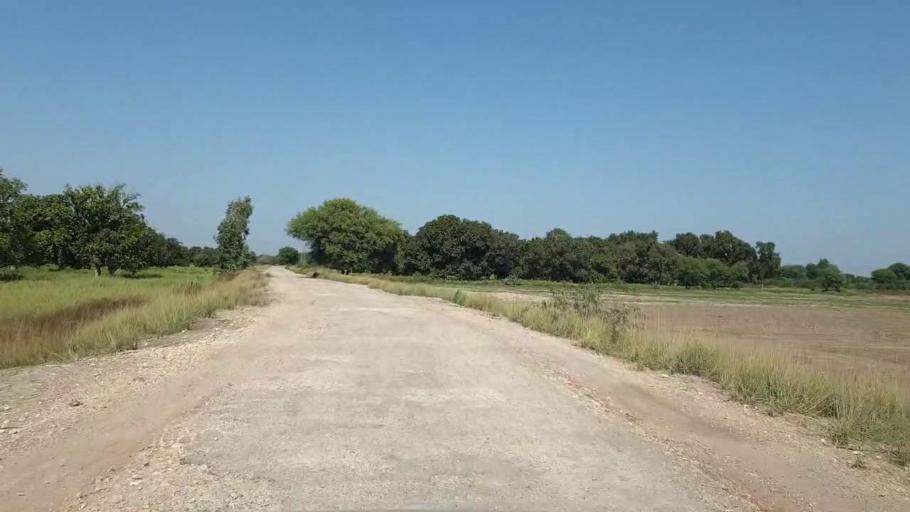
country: PK
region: Sindh
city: Tando Jam
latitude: 25.4226
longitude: 68.4586
